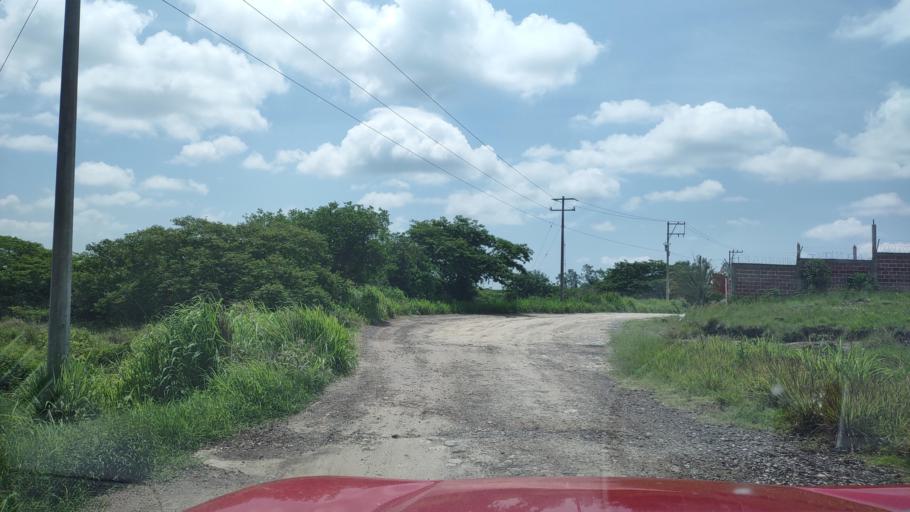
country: MX
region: Veracruz
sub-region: Emiliano Zapata
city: Dos Rios
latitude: 19.4634
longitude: -96.7919
